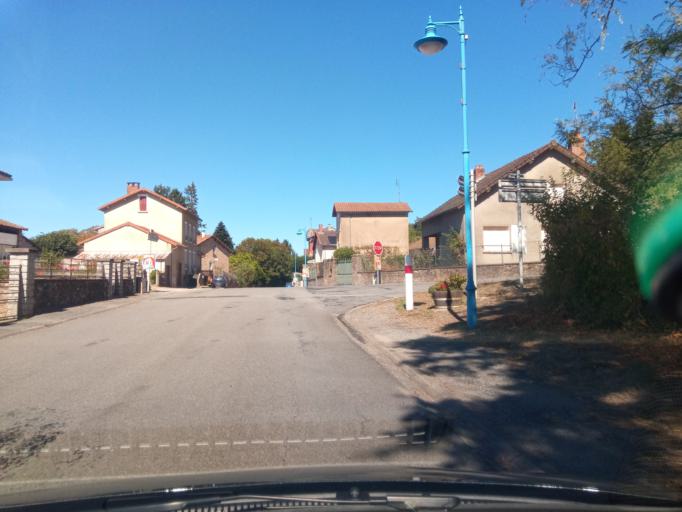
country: FR
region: Limousin
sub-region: Departement de la Haute-Vienne
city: Nantiat
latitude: 46.0740
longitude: 1.2024
